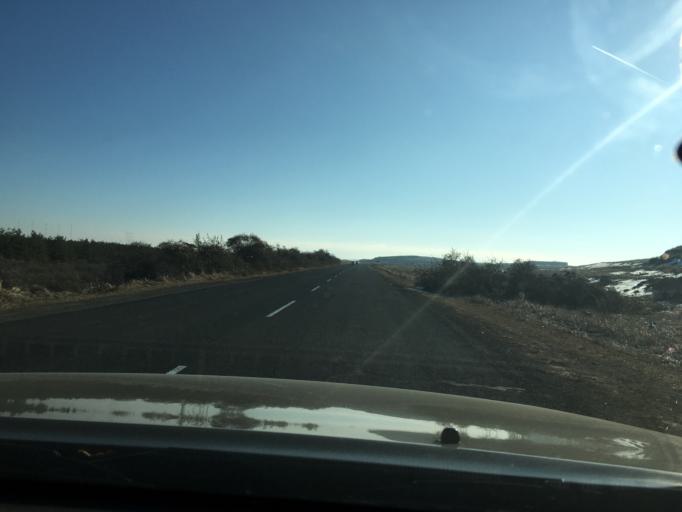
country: AM
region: Geghark'unik'i Marz
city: Gavarr
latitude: 40.4036
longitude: 45.1332
